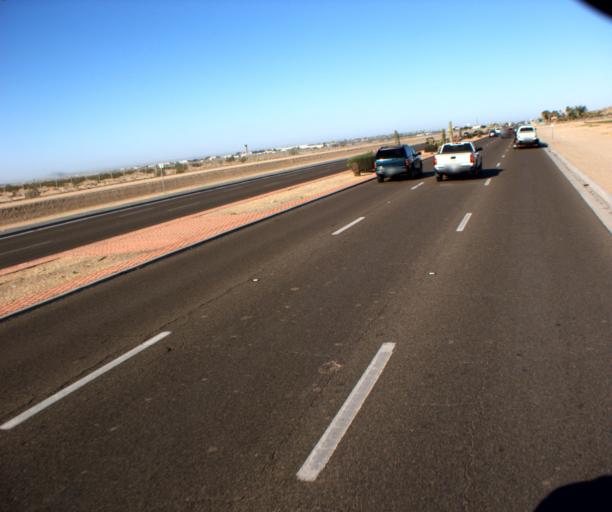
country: US
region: Arizona
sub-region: Yuma County
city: Yuma
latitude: 32.6697
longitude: -114.5862
